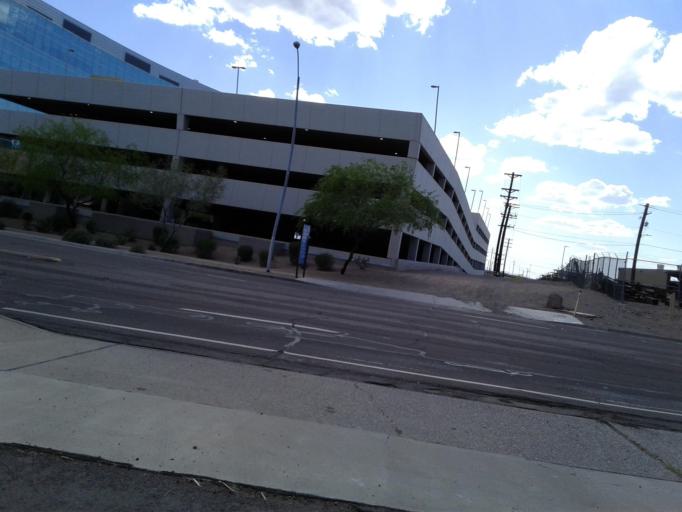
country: US
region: Arizona
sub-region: Maricopa County
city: Tempe Junction
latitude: 33.4388
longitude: -111.9435
